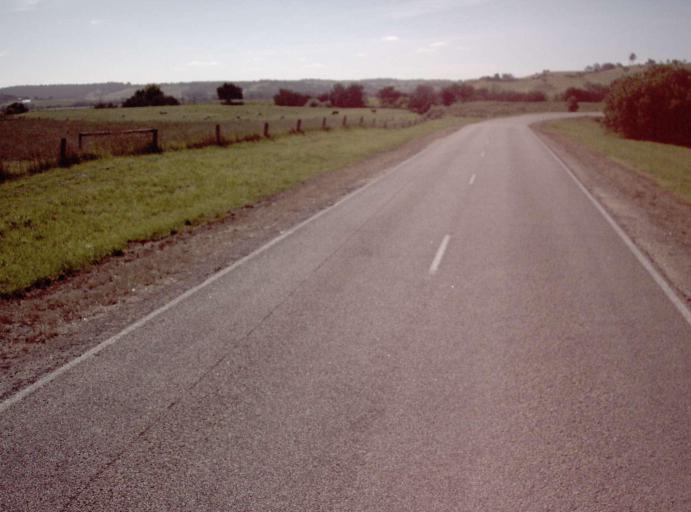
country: AU
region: Victoria
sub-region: East Gippsland
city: Lakes Entrance
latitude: -37.7391
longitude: 147.8166
